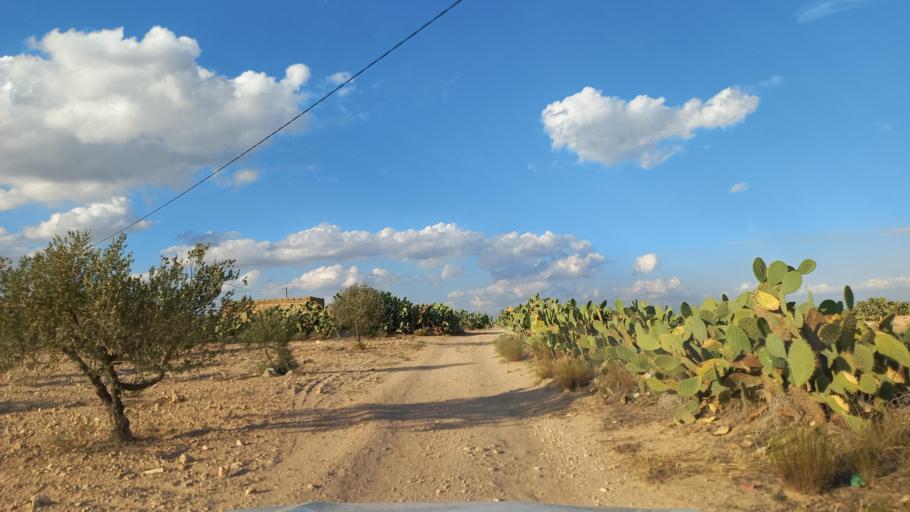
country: TN
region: Al Qasrayn
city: Sbiba
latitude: 35.3914
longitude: 9.0537
